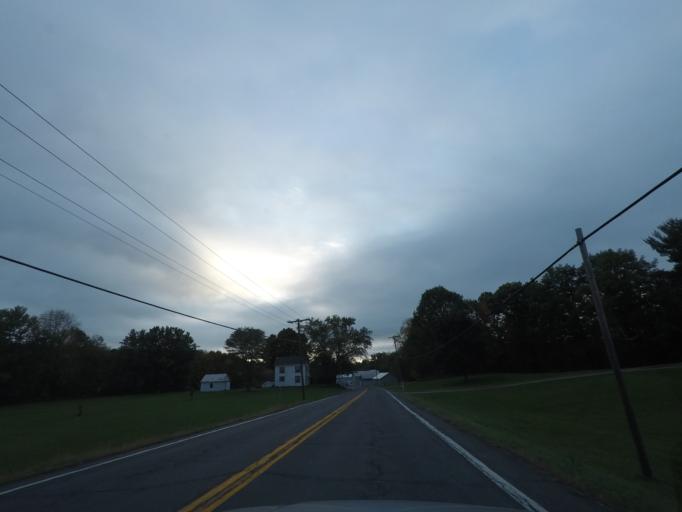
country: US
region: New York
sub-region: Rensselaer County
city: East Greenbush
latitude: 42.5554
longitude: -73.6643
